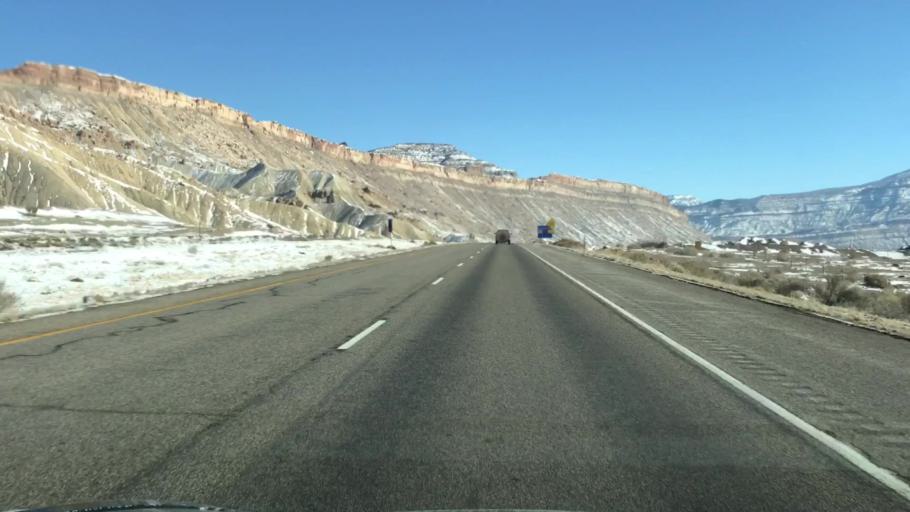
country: US
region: Colorado
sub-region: Mesa County
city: Palisade
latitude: 39.1147
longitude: -108.4010
